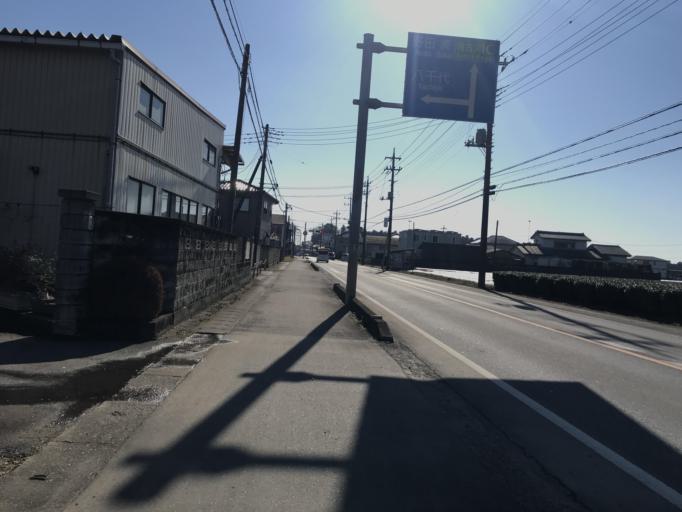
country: JP
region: Ibaraki
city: Sakai
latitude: 36.1563
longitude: 139.8103
